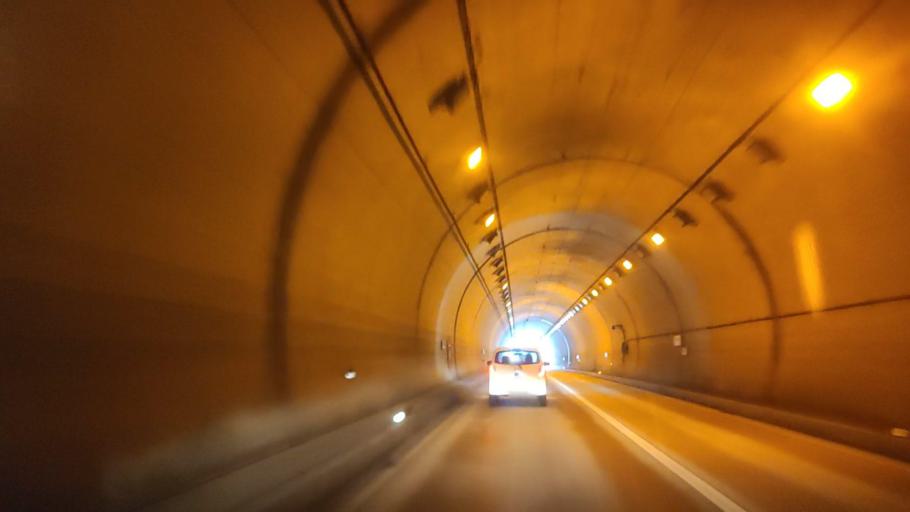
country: JP
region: Tottori
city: Kurayoshi
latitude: 35.3015
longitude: 133.7390
